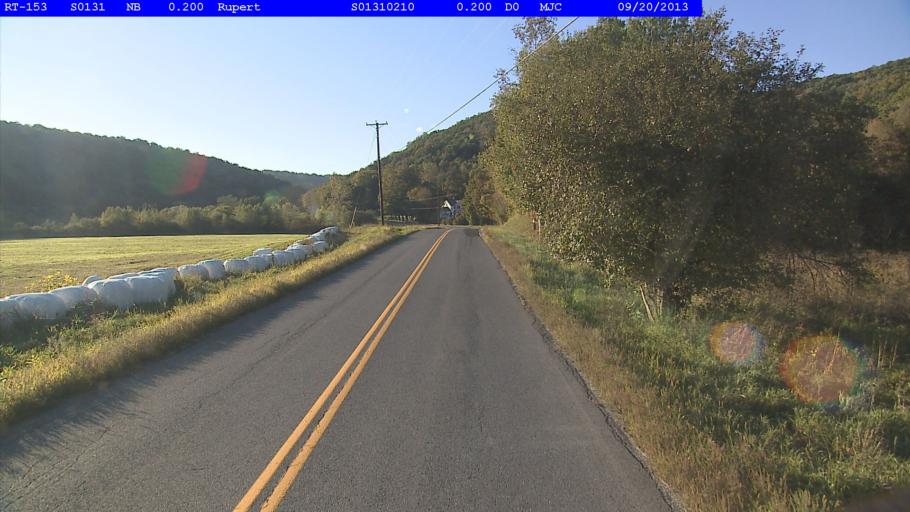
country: US
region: New York
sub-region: Washington County
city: Granville
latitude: 43.2619
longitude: -73.2256
